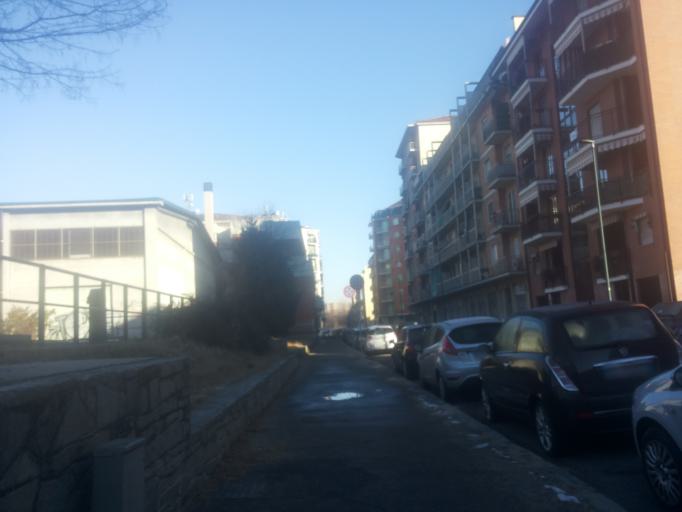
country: IT
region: Piedmont
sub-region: Provincia di Torino
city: Lesna
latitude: 45.0584
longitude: 7.6499
